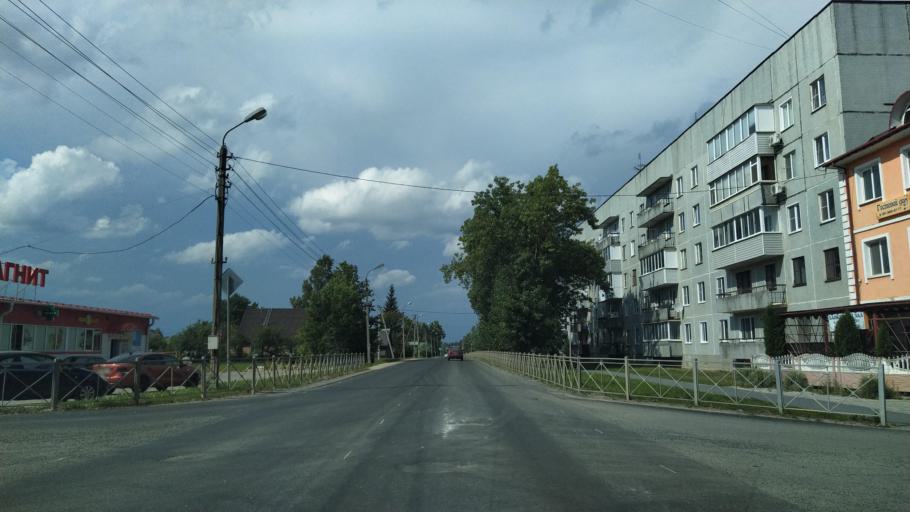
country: RU
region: Pskov
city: Porkhov
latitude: 57.7628
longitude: 29.5559
